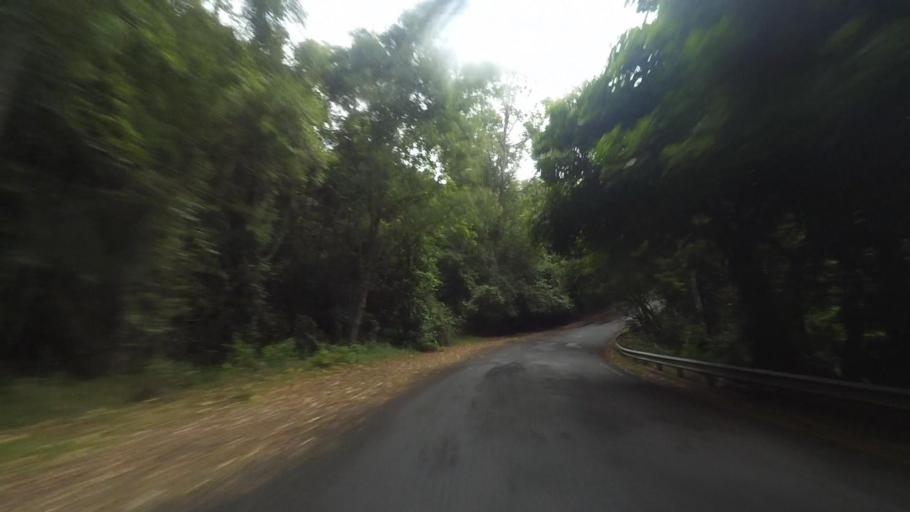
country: AU
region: New South Wales
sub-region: Wollongong
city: Cordeaux Heights
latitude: -34.4148
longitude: 150.8174
